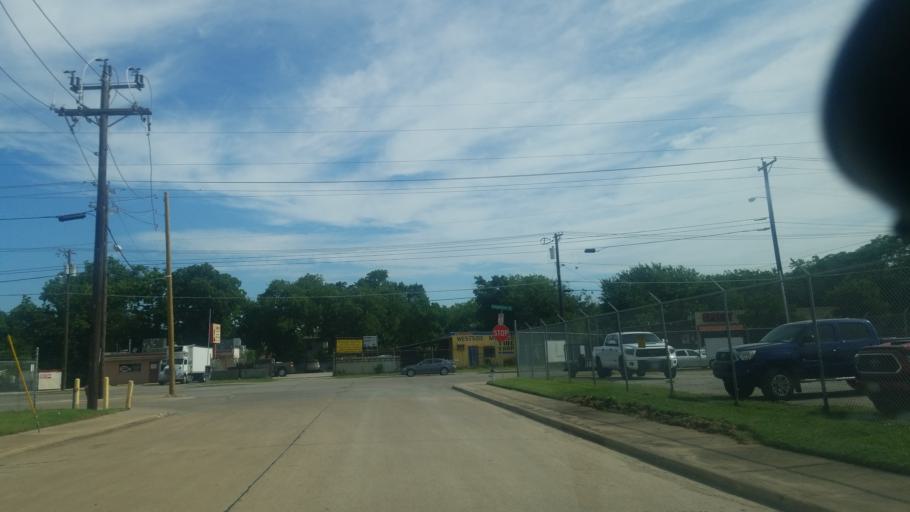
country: US
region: Texas
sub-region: Dallas County
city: Dallas
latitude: 32.7781
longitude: -96.8529
